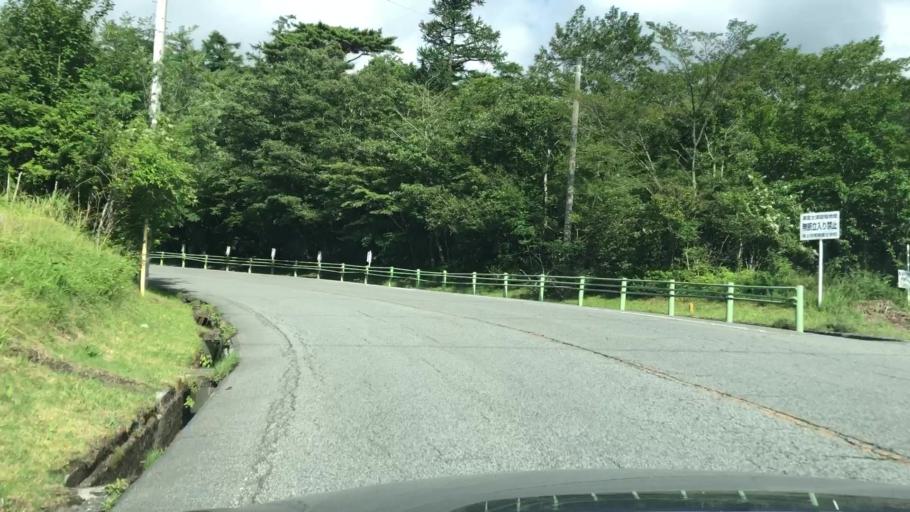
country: JP
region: Shizuoka
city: Gotemba
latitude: 35.3332
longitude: 138.8088
